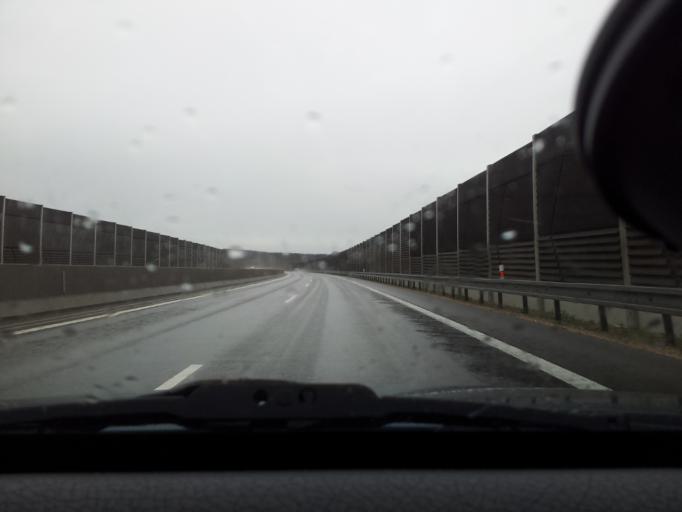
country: SK
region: Nitriansky
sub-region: Okres Nitra
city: Nitra
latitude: 48.2939
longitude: 18.0389
